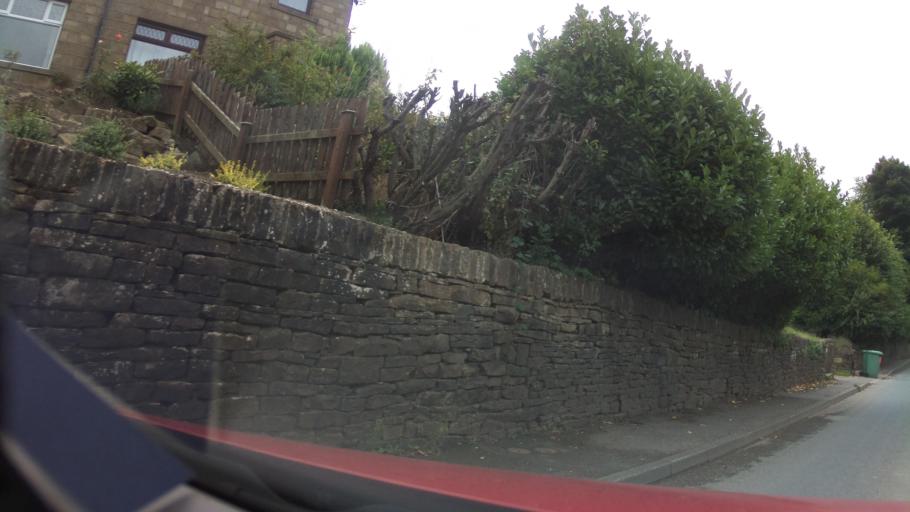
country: GB
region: England
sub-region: Kirklees
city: Holmfirth
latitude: 53.5783
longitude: -1.7779
